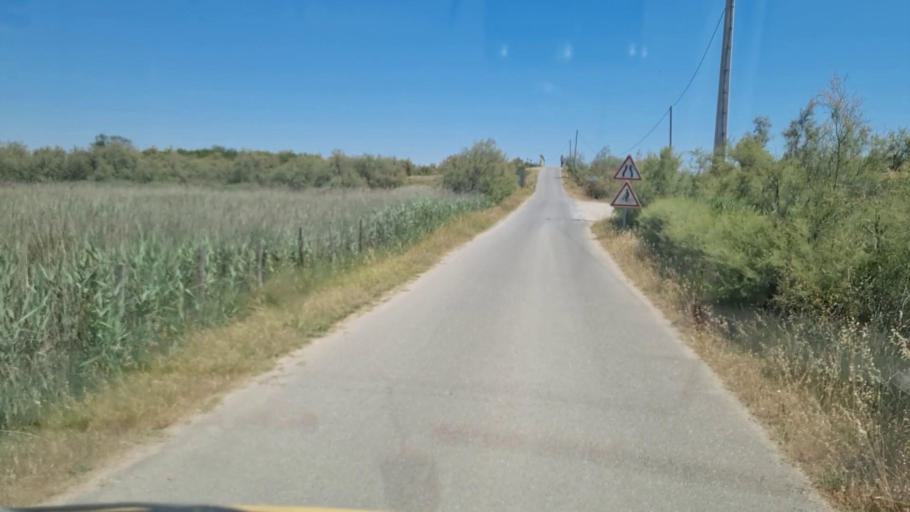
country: FR
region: Languedoc-Roussillon
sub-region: Departement du Gard
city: Le Cailar
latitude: 43.6204
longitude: 4.2581
